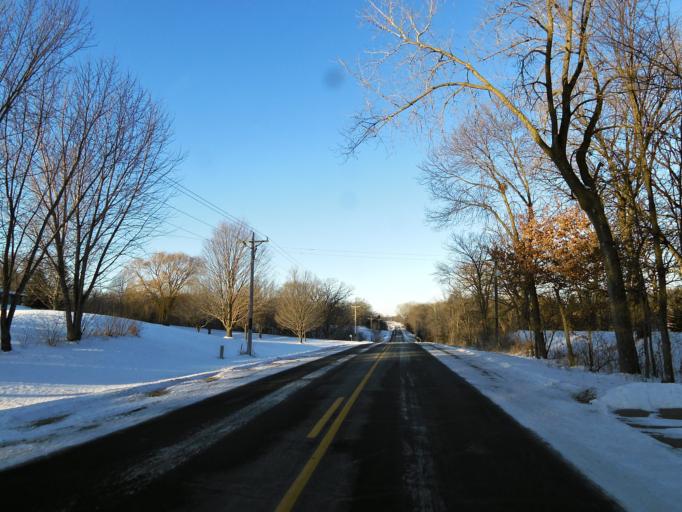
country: US
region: Minnesota
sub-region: Scott County
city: Prior Lake
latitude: 44.6741
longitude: -93.4506
